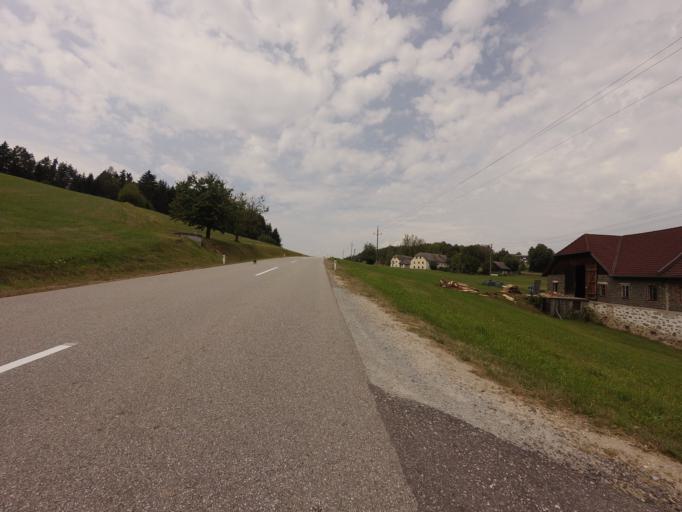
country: AT
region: Upper Austria
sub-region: Politischer Bezirk Urfahr-Umgebung
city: Reichenthal
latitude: 48.5558
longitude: 14.4139
